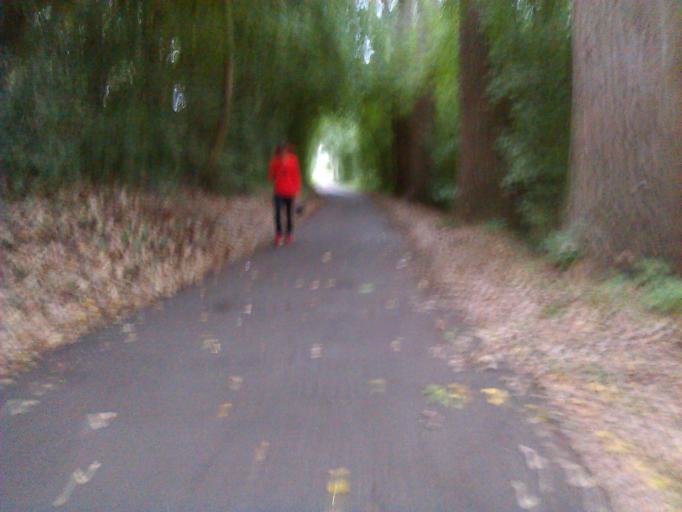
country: DE
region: Baden-Wuerttemberg
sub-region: Regierungsbezirk Stuttgart
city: Nurtingen
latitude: 48.6190
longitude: 9.3168
